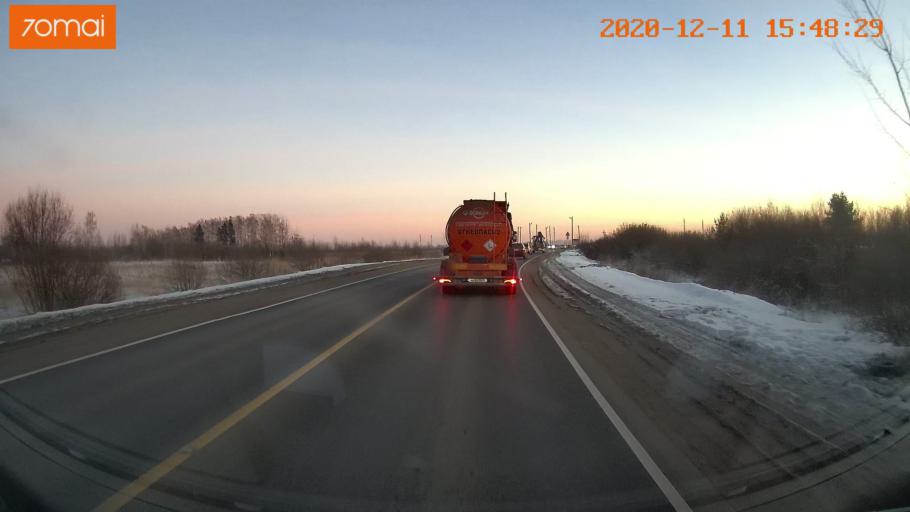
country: RU
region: Ivanovo
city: Novo-Talitsy
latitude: 56.9924
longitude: 40.8688
